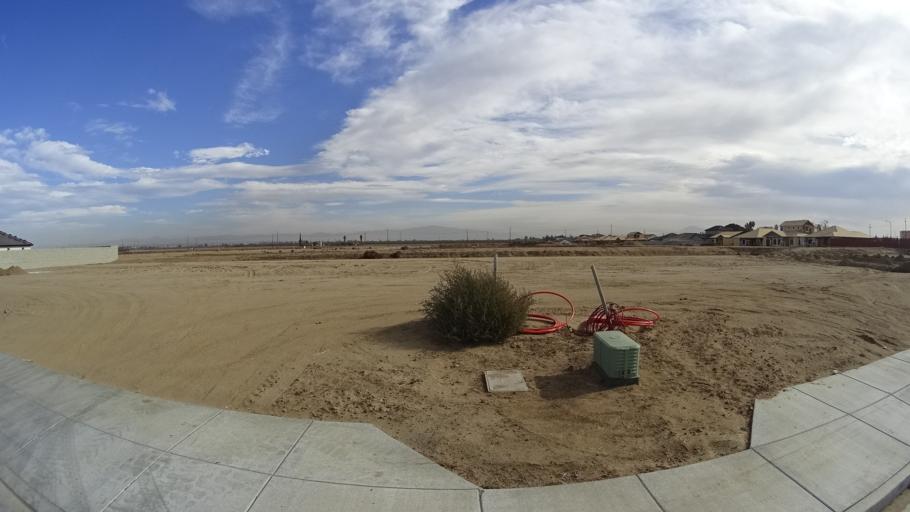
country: US
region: California
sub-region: Kern County
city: Greenacres
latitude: 35.4288
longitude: -119.0995
